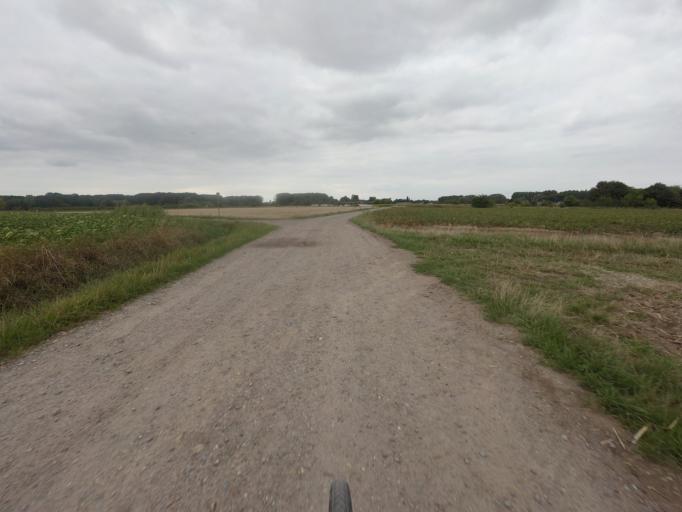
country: BE
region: Flanders
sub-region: Provincie Vlaams-Brabant
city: Herent
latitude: 50.9108
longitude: 4.6522
